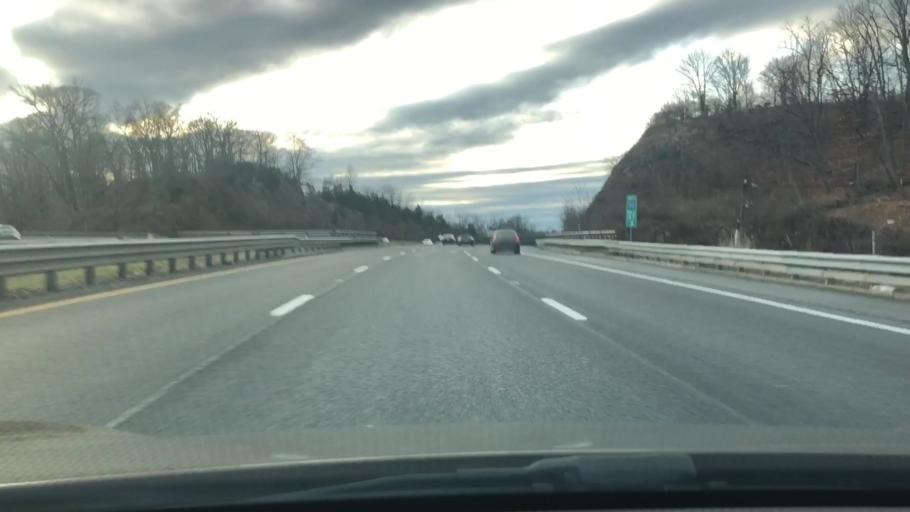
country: US
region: New Jersey
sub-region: Essex County
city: Fairfield
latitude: 40.8619
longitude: -74.3391
